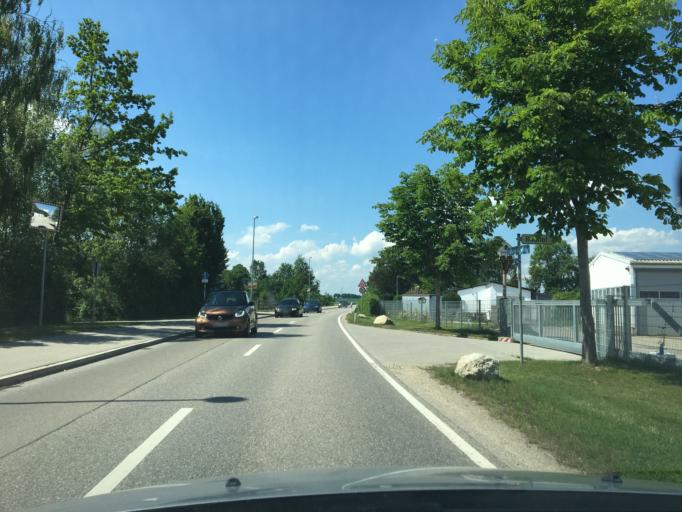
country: DE
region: Bavaria
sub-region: Upper Bavaria
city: Haimhausen
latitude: 48.3181
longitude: 11.5500
